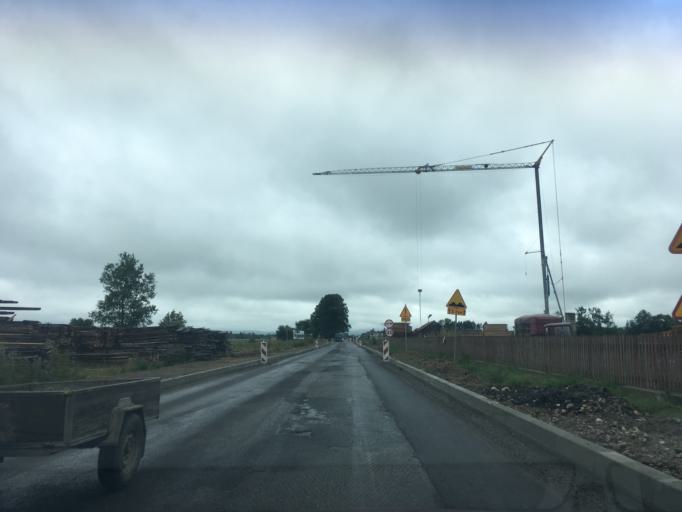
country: PL
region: Lesser Poland Voivodeship
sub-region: Powiat nowotarski
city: Czarny Dunajec
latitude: 49.4158
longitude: 19.8344
